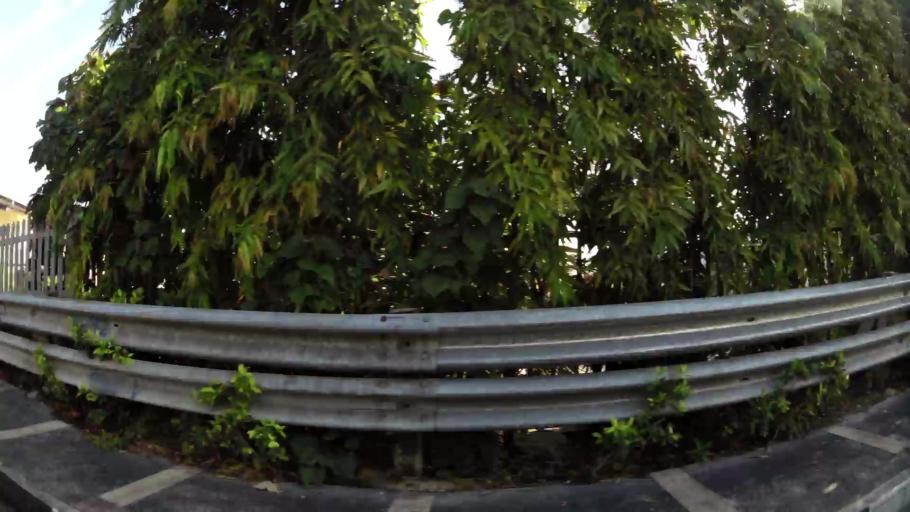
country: SG
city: Singapore
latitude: 1.3182
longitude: 103.9214
